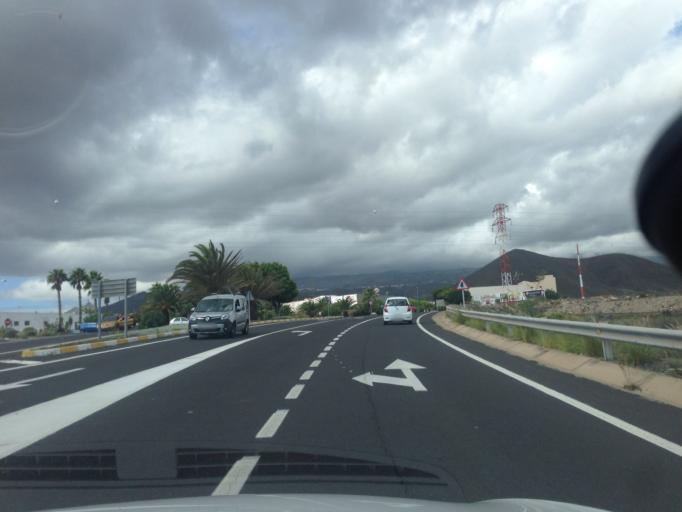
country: ES
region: Canary Islands
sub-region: Provincia de Santa Cruz de Tenerife
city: San Miguel
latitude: 28.0467
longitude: -16.6103
